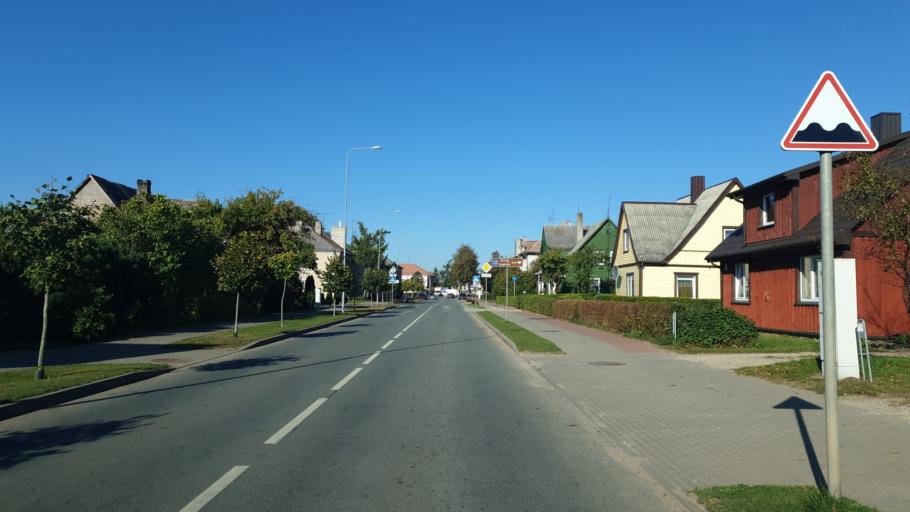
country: LT
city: Varniai
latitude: 55.7408
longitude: 22.3750
